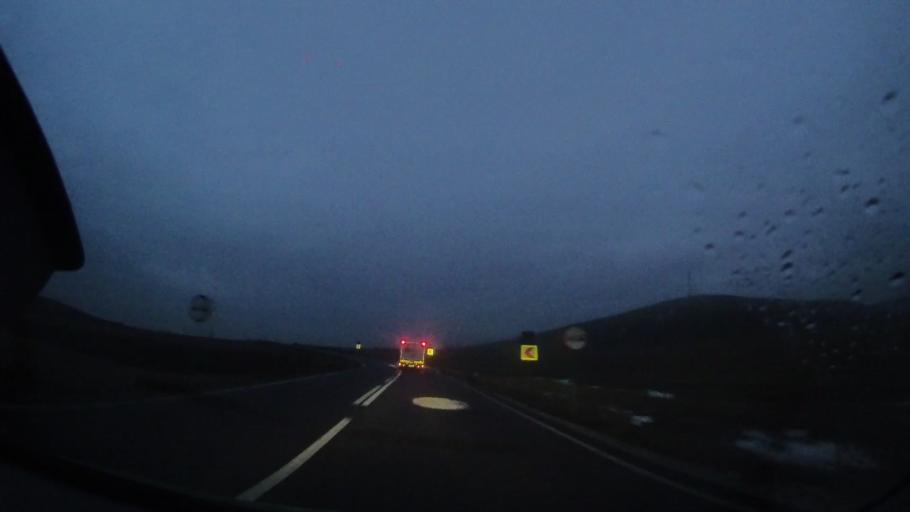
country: RO
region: Harghita
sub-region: Comuna Subcetate
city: Subcetate
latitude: 46.8442
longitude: 25.4723
